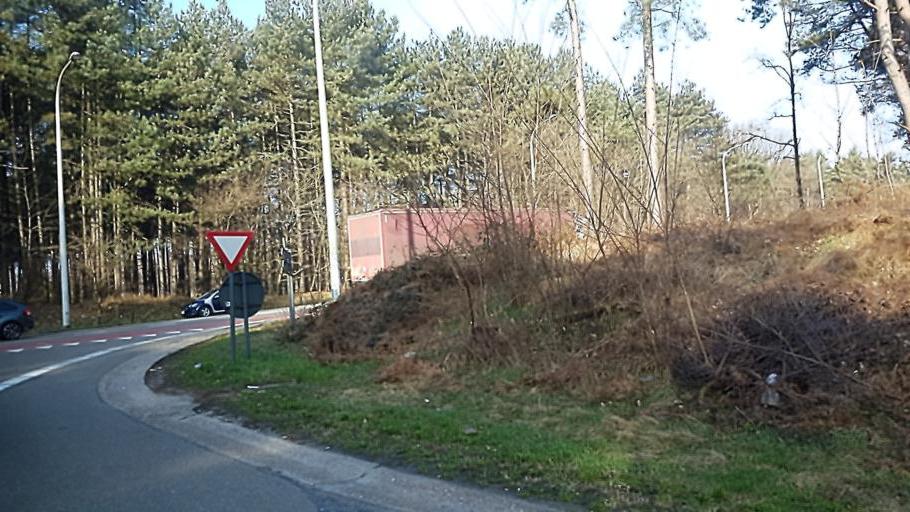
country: BE
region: Flanders
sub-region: Provincie Limburg
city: Genk
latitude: 51.0009
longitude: 5.4584
